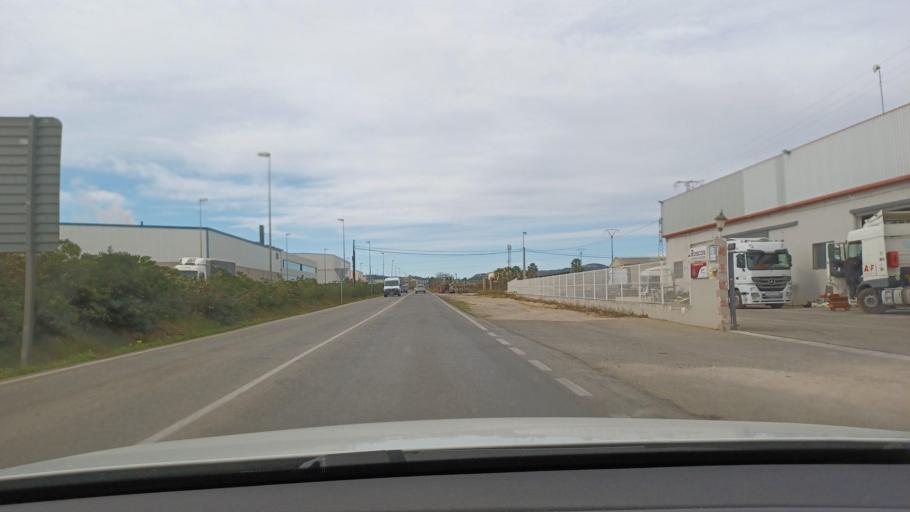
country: ES
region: Valencia
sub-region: Provincia de Valencia
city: Benifaio
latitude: 39.2884
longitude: -0.4427
